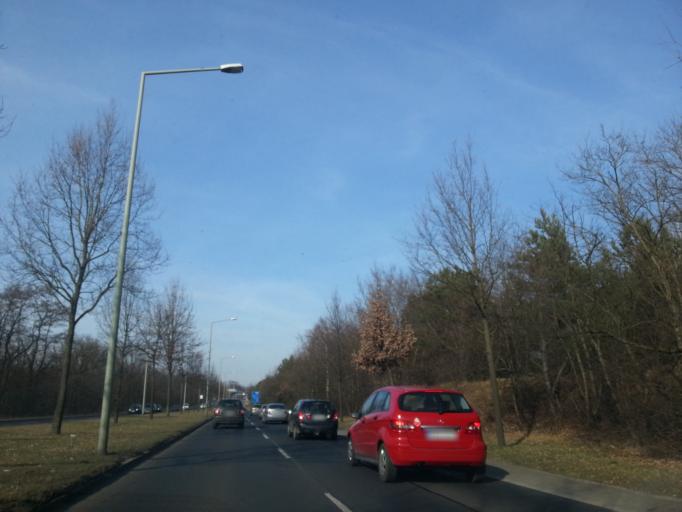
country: DE
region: Saxony
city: Albertstadt
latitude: 51.1010
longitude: 13.7357
